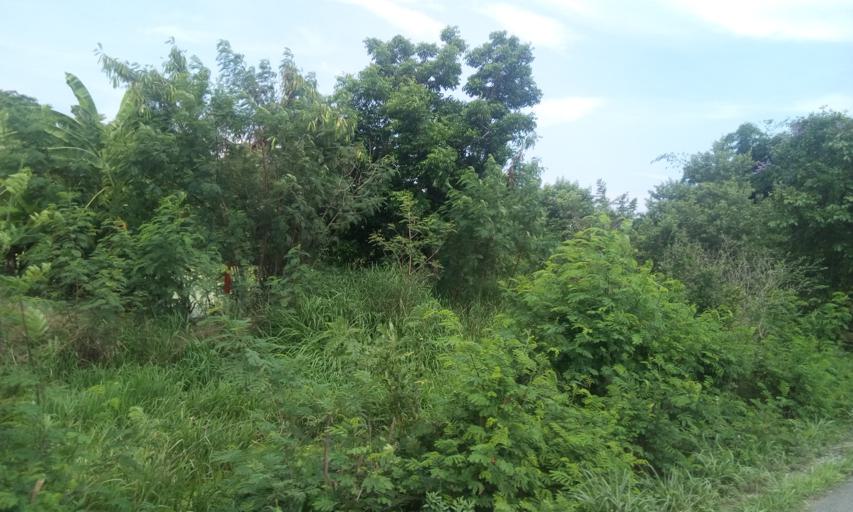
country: TH
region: Pathum Thani
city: Ban Lam Luk Ka
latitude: 14.0245
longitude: 100.8436
